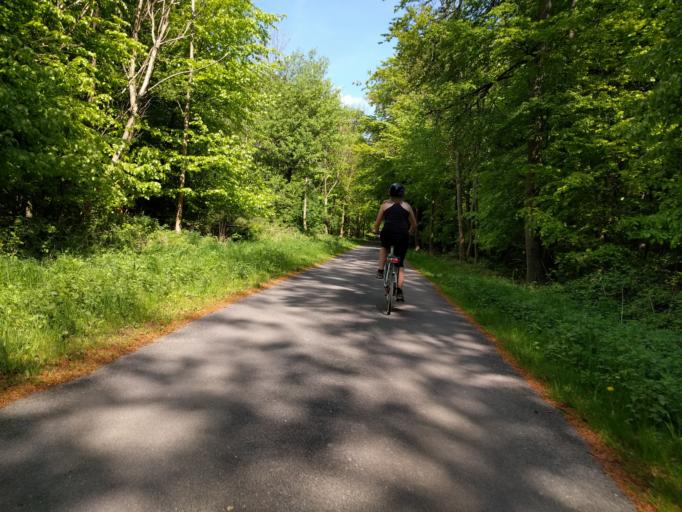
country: DK
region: Zealand
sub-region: Guldborgsund Kommune
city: Stubbekobing
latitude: 54.7920
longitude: 12.0881
